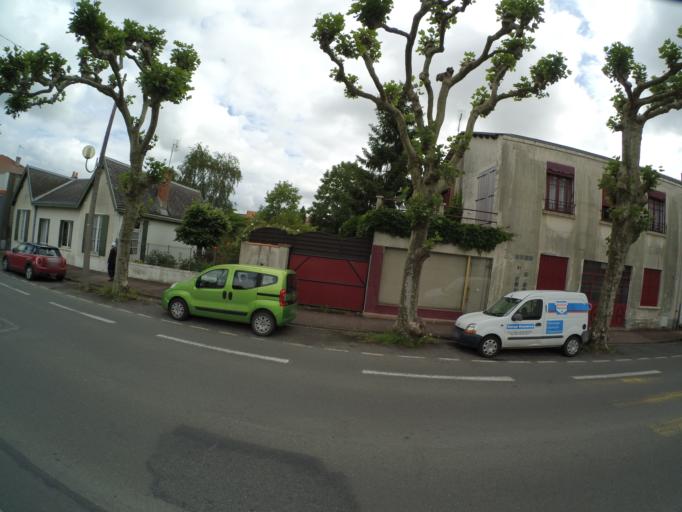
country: FR
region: Poitou-Charentes
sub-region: Departement de la Charente-Maritime
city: Rochefort
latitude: 45.9458
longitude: -0.9626
